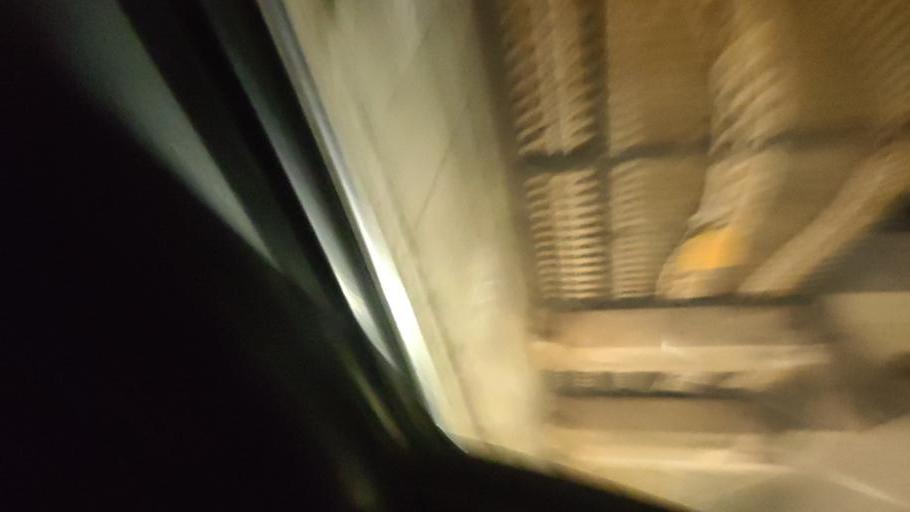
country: IN
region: Telangana
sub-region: Hyderabad
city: Hyderabad
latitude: 17.3274
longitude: 78.4268
